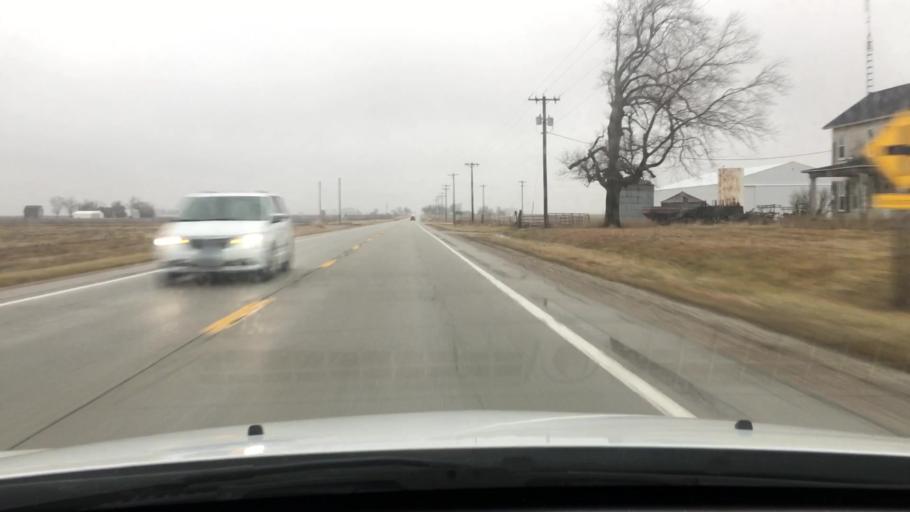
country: US
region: Illinois
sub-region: Livingston County
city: Flanagan
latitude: 40.8721
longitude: -88.7746
